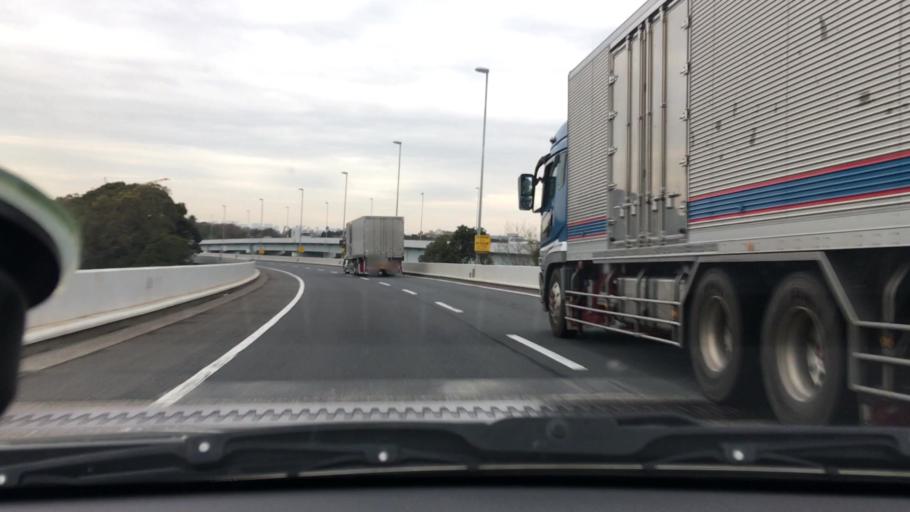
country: JP
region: Kanagawa
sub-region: Kawasaki-shi
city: Kawasaki
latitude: 35.5807
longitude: 139.7585
